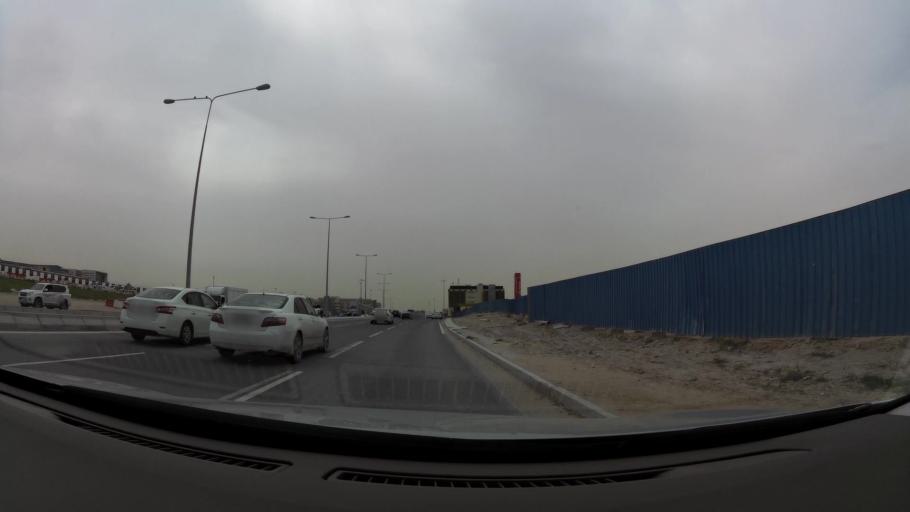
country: QA
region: Baladiyat ad Dawhah
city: Doha
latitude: 25.3032
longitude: 51.5109
